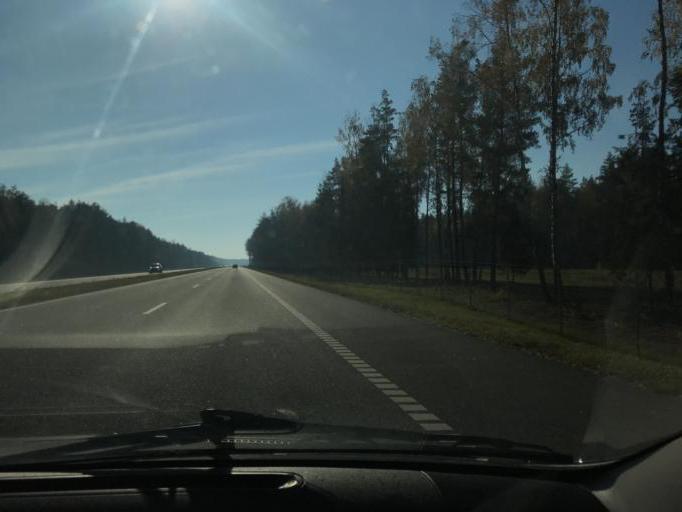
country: BY
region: Minsk
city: Slutsk
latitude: 53.3060
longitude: 27.5410
